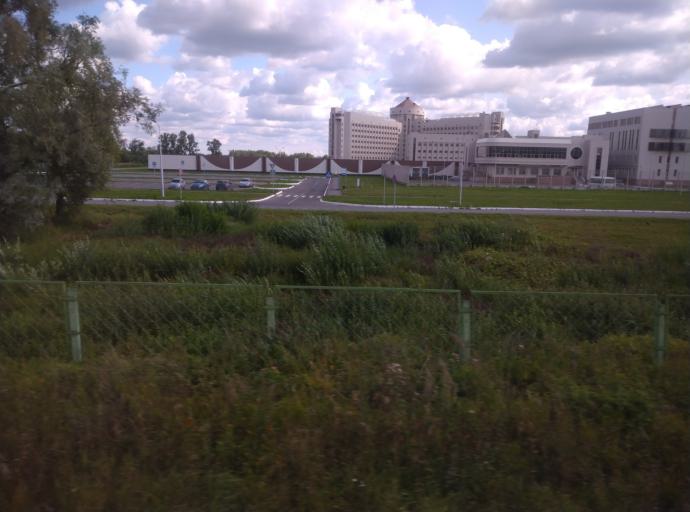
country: RU
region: St.-Petersburg
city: Kolpino
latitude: 59.7392
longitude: 30.6272
